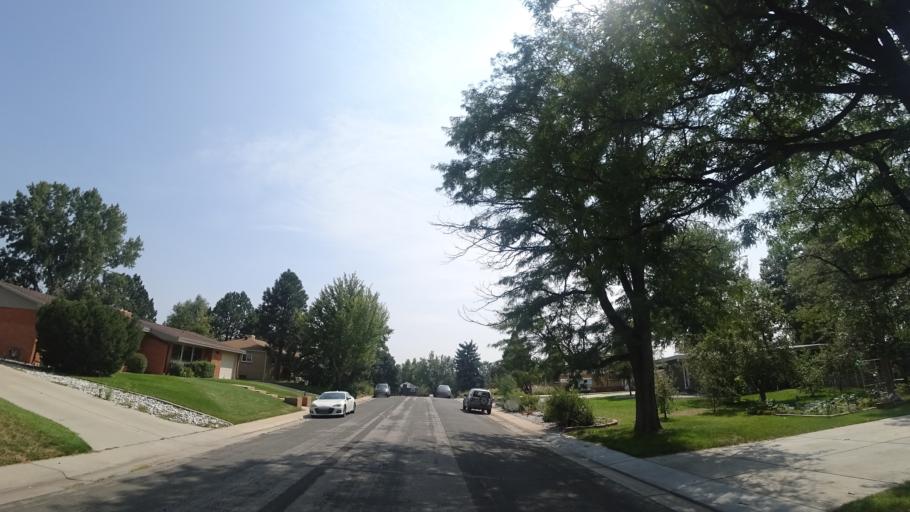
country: US
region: Colorado
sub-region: Arapahoe County
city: Englewood
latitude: 39.6288
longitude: -104.9985
